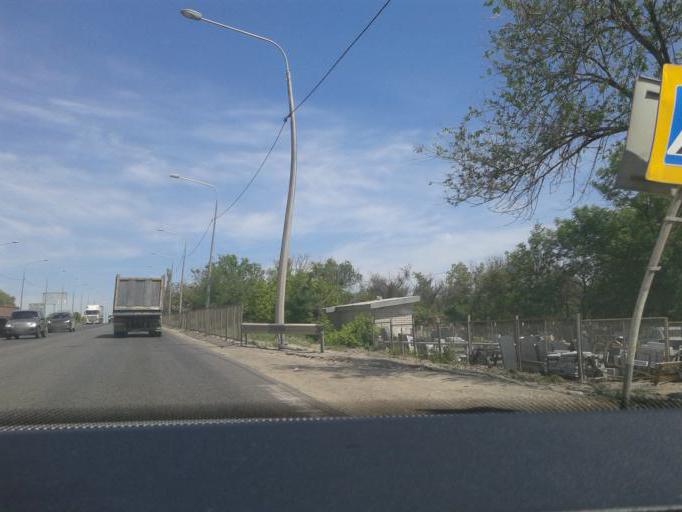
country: RU
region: Volgograd
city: Gorodishche
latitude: 48.7805
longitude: 44.5201
